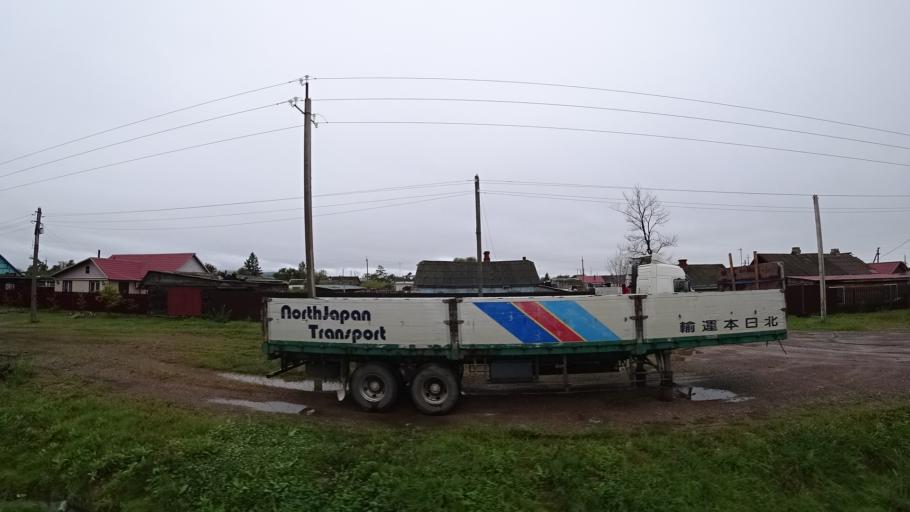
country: RU
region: Primorskiy
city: Monastyrishche
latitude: 44.2016
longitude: 132.4620
